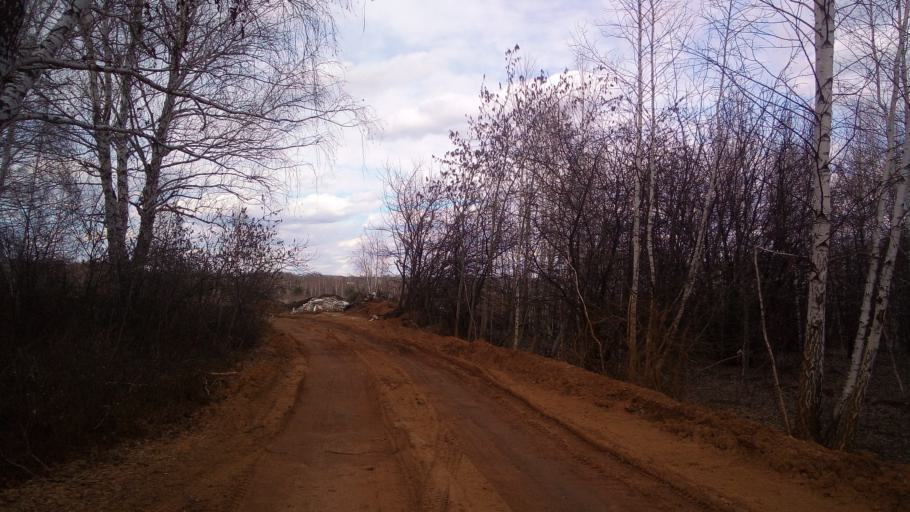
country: RU
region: Chelyabinsk
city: Sargazy
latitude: 55.1247
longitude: 61.2585
